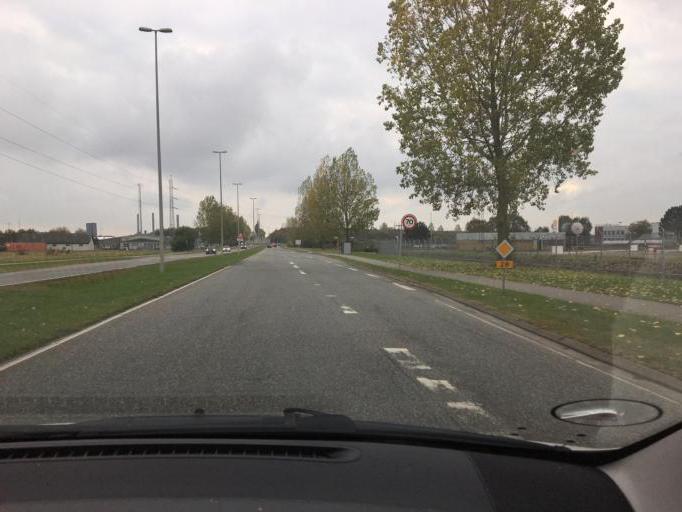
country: DK
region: South Denmark
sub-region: Fredericia Kommune
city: Fredericia
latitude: 55.5925
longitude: 9.7552
